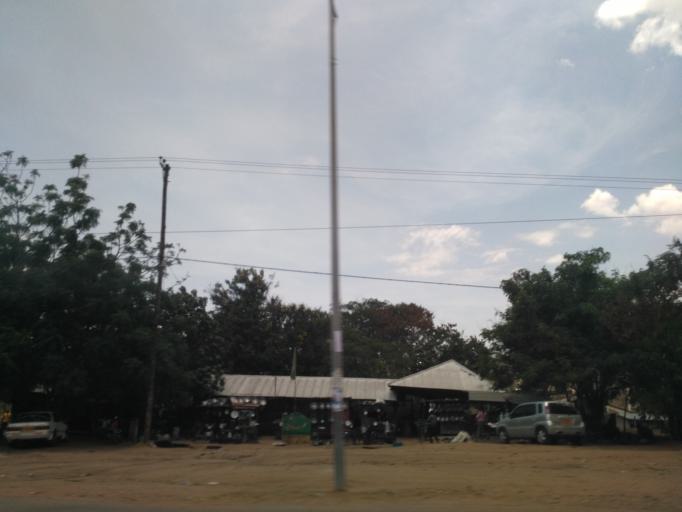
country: TZ
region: Mwanza
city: Mwanza
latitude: -2.5671
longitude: 32.9187
